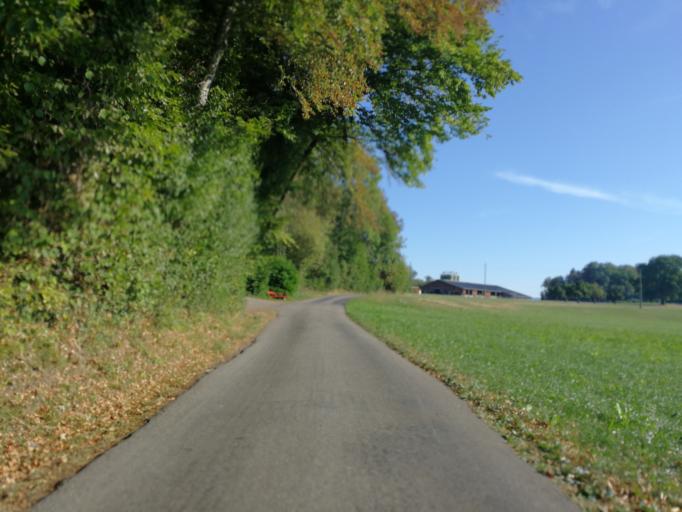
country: CH
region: Zurich
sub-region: Bezirk Hinwil
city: Wolfhausen
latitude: 47.2574
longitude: 8.7897
